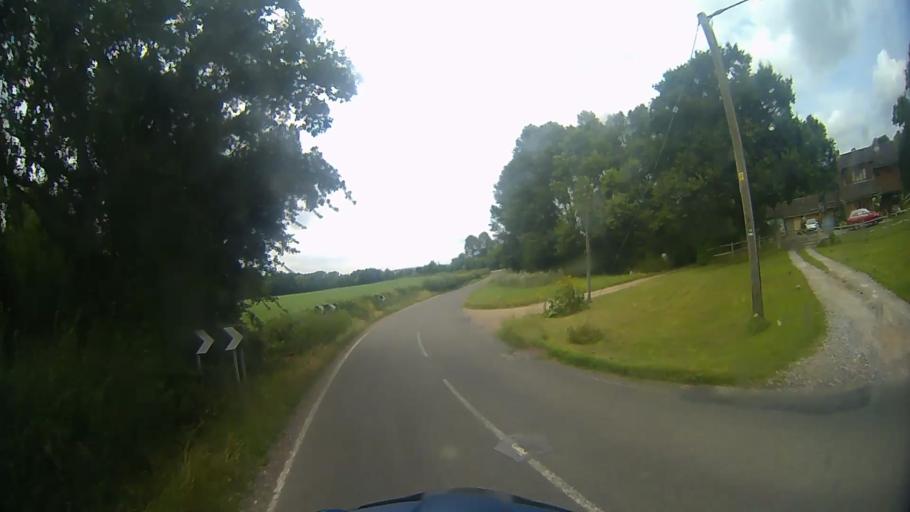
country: GB
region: England
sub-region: Hampshire
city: Kingsley
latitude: 51.1753
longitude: -0.8689
